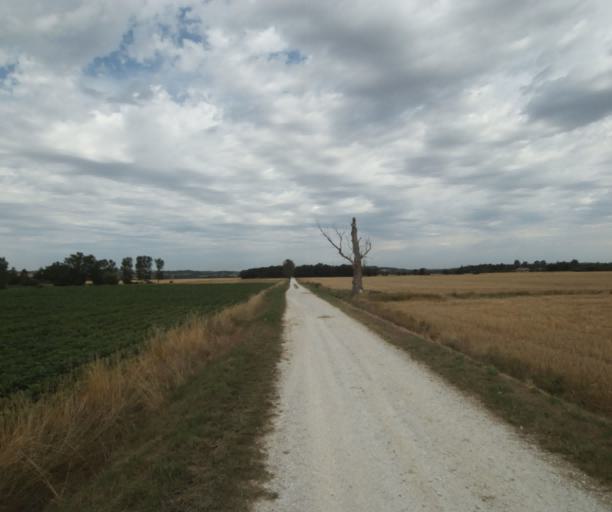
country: FR
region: Midi-Pyrenees
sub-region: Departement de la Haute-Garonne
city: Saint-Felix-Lauragais
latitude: 43.4366
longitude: 1.9441
